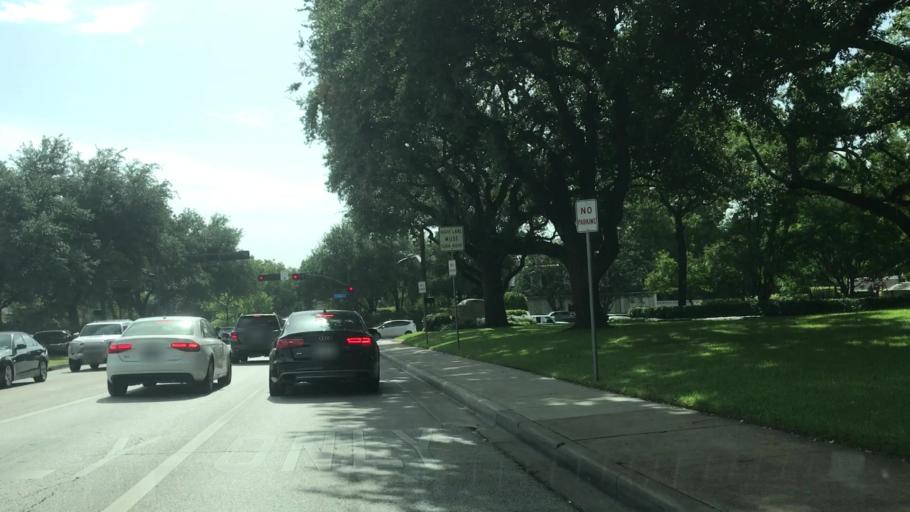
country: US
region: Texas
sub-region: Dallas County
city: Highland Park
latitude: 32.8366
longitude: -96.7864
